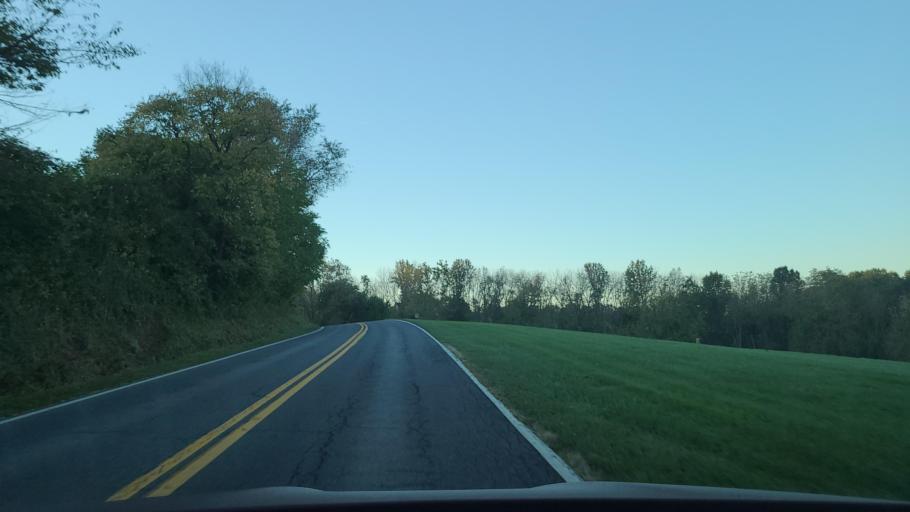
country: US
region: Maryland
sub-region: Frederick County
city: Jefferson
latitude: 39.3839
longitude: -77.5384
